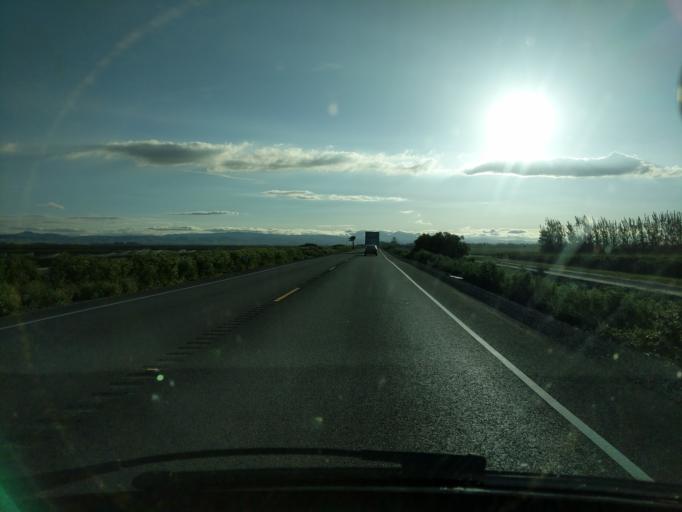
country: US
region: California
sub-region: Contra Costa County
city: Discovery Bay
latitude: 37.8914
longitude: -121.4976
